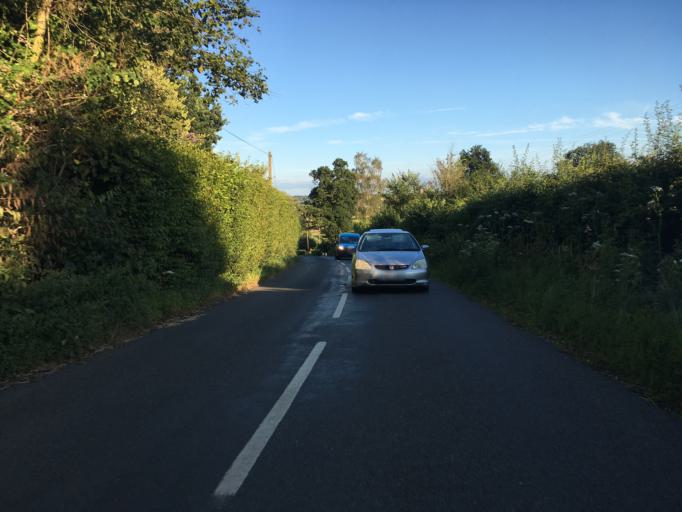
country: GB
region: England
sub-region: Hampshire
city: Tadley
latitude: 51.4153
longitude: -1.1445
